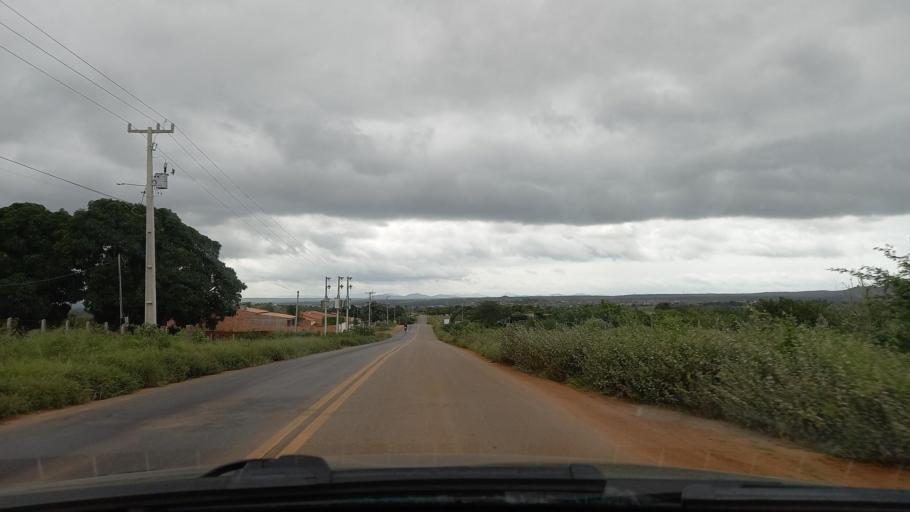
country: BR
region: Sergipe
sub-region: Caninde De Sao Francisco
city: Caninde de Sao Francisco
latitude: -9.6831
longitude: -37.8118
